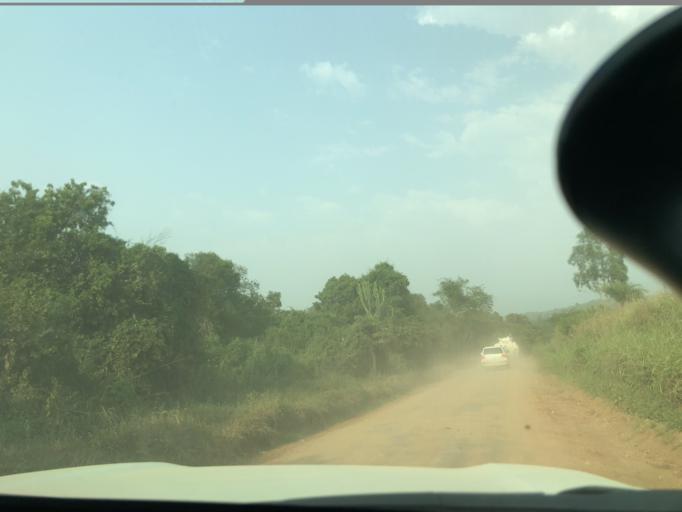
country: UG
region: Western Region
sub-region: Kasese District
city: Margherita
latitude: 0.1732
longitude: 29.6506
